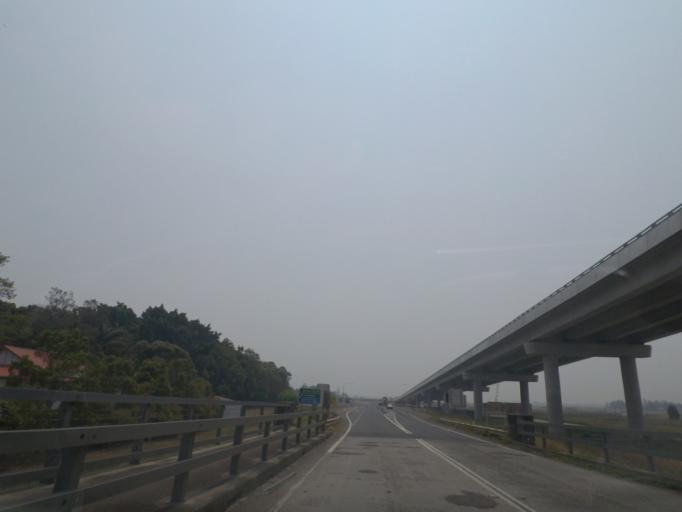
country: AU
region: New South Wales
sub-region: Clarence Valley
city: Maclean
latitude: -29.4265
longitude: 153.2412
